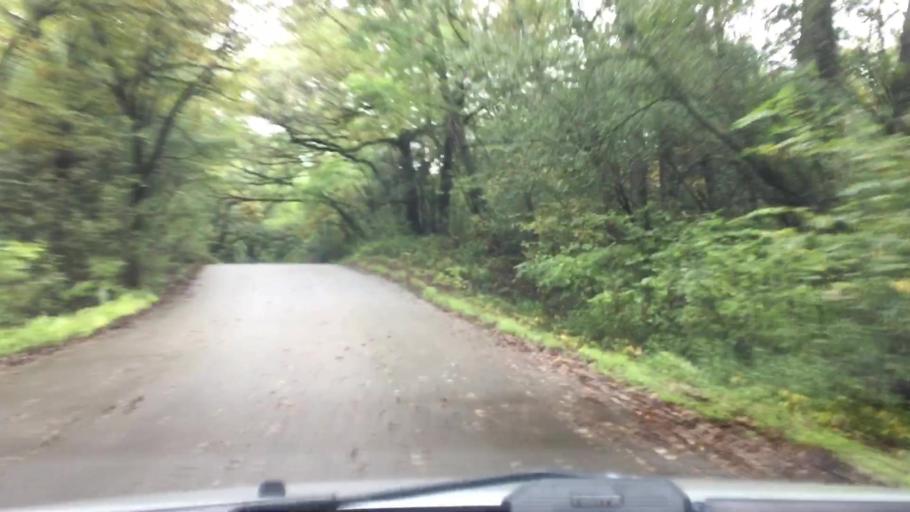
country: US
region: Wisconsin
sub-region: Waukesha County
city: Eagle
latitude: 42.9257
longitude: -88.4599
